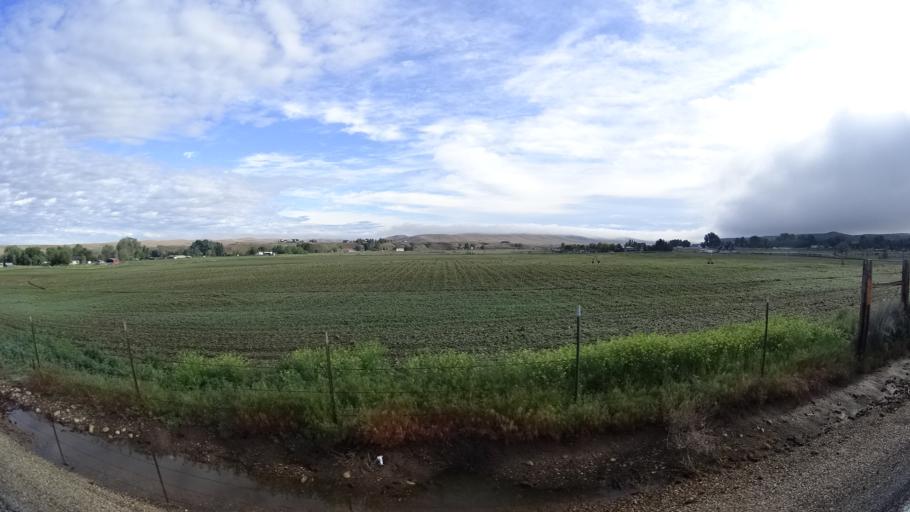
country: US
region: Idaho
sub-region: Ada County
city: Star
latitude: 43.7717
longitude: -116.4760
